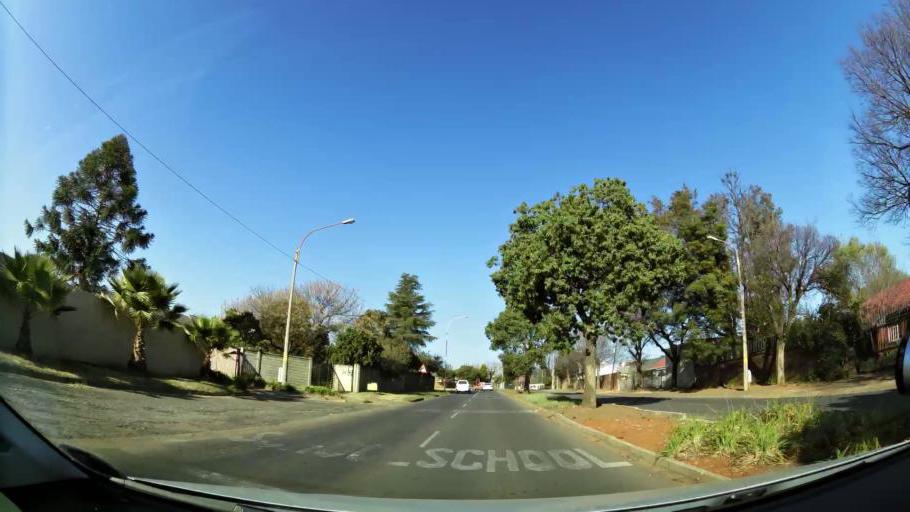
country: ZA
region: Gauteng
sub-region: City of Johannesburg Metropolitan Municipality
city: Modderfontein
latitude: -26.1512
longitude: 28.1627
